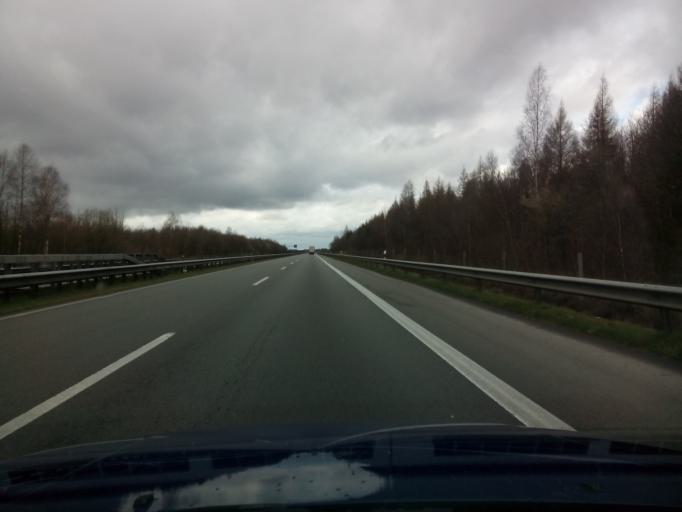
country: DE
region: Lower Saxony
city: Haren
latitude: 52.7218
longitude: 7.1511
